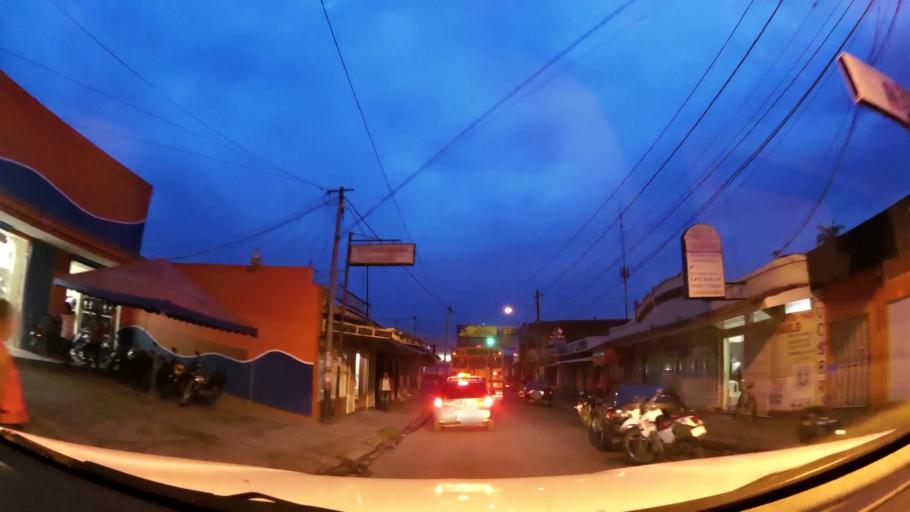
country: NI
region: Esteli
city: Esteli
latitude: 13.0869
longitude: -86.3564
